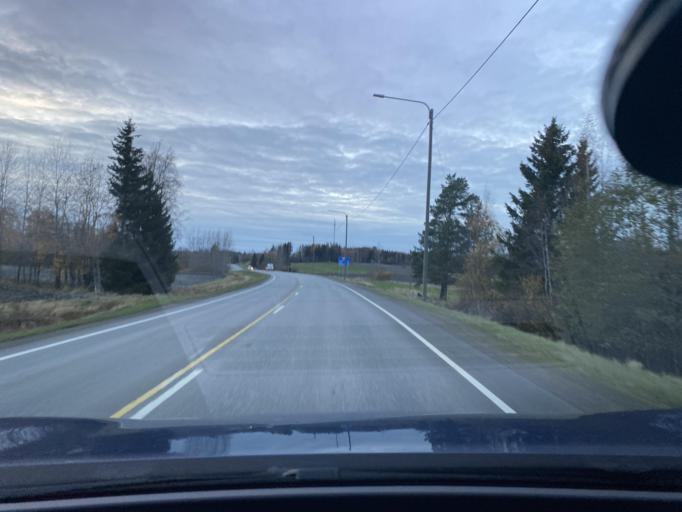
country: FI
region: Uusimaa
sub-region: Helsinki
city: Lohja
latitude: 60.3680
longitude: 24.1587
